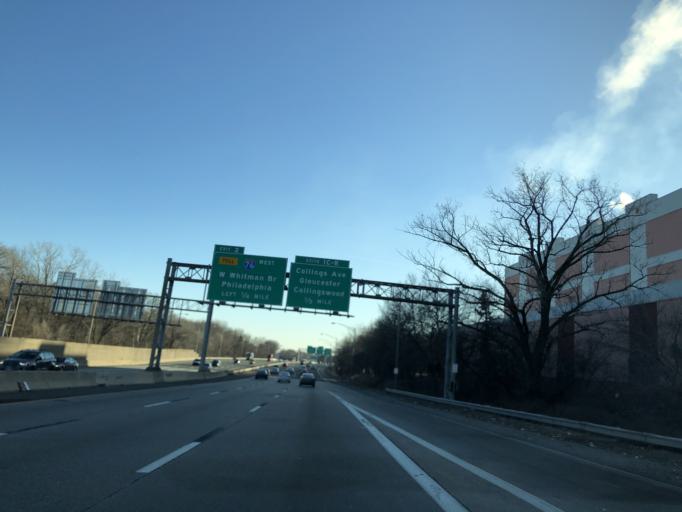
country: US
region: New Jersey
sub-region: Camden County
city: Camden
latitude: 39.9108
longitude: -75.1156
